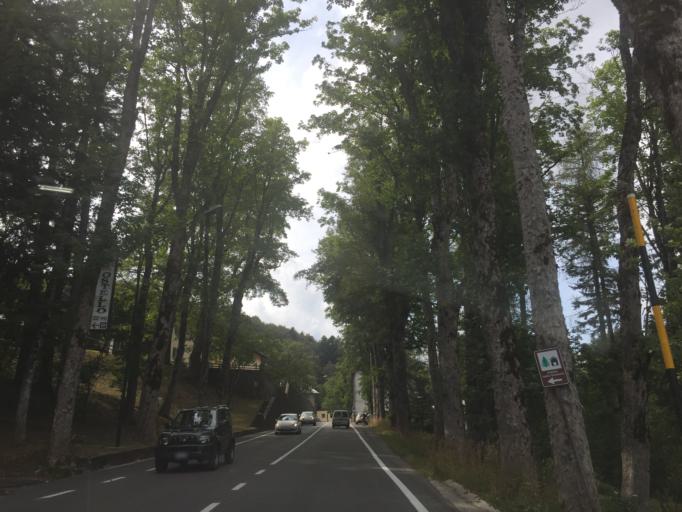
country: IT
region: Tuscany
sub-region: Provincia di Pistoia
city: Abetone
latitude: 44.1392
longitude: 10.6752
